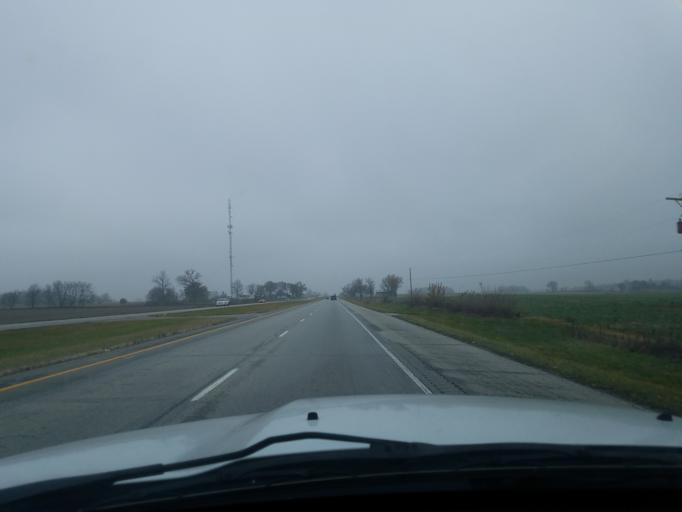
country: US
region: Indiana
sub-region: Hamilton County
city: Arcadia
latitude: 40.1944
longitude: -86.1279
